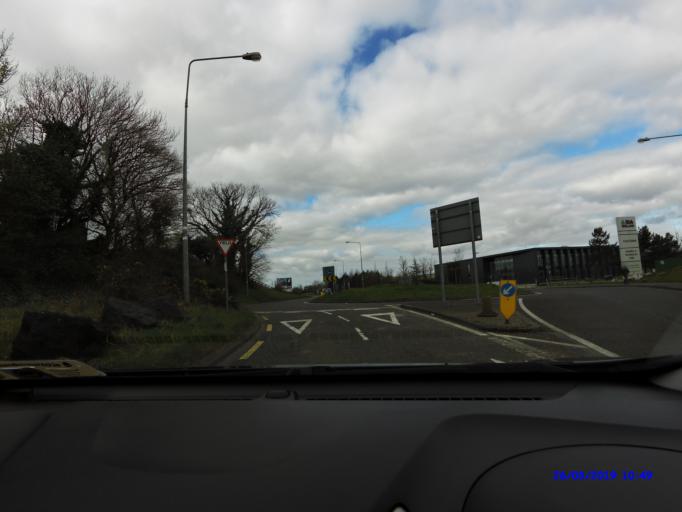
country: IE
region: Connaught
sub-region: Maigh Eo
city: Castlebar
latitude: 53.8504
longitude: -9.2741
